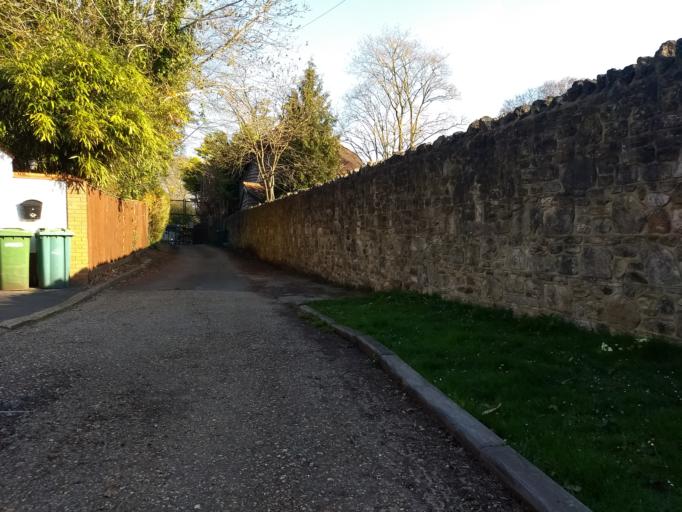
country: GB
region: England
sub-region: Isle of Wight
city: Ryde
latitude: 50.7279
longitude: -1.1836
